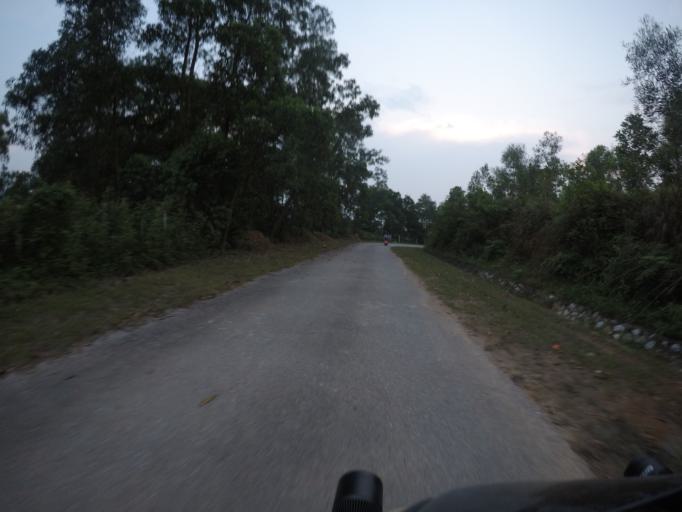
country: VN
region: Thai Nguyen
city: Chua Hang
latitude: 21.5819
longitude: 105.7129
